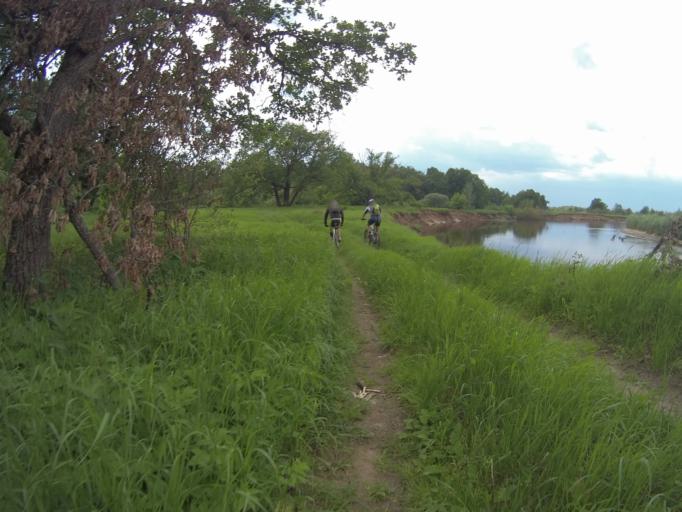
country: RU
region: Vladimir
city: Vorsha
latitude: 56.0336
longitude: 40.1990
